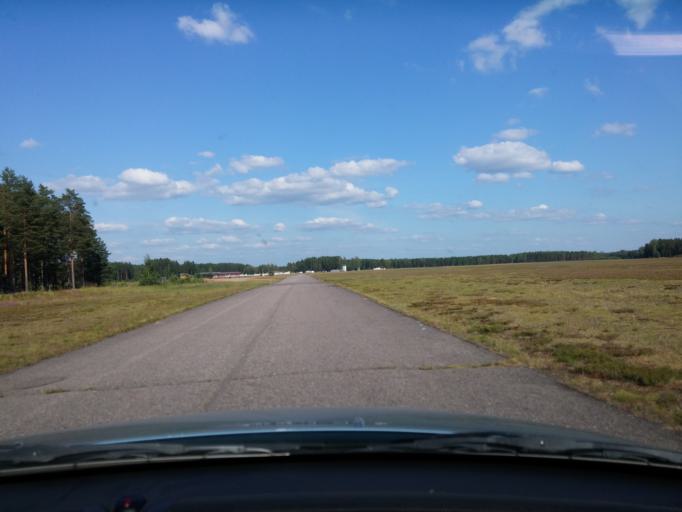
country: FI
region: Uusimaa
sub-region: Helsinki
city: Kaerkoelae
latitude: 60.7433
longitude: 24.1009
